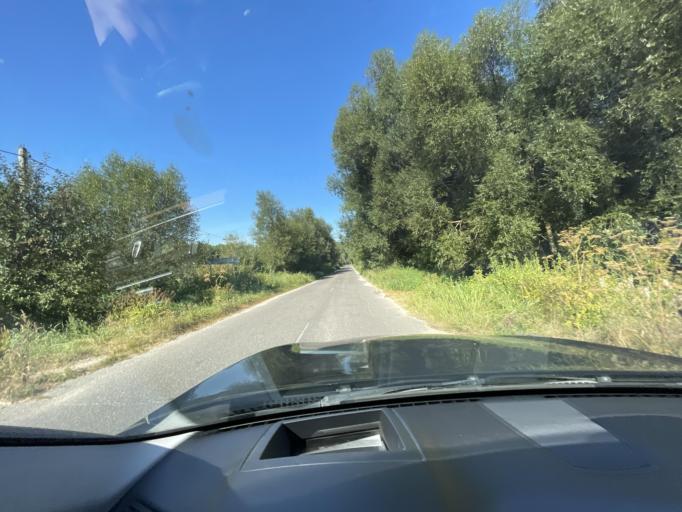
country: BY
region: Grodnenskaya
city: Hrodna
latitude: 53.7483
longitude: 23.9763
